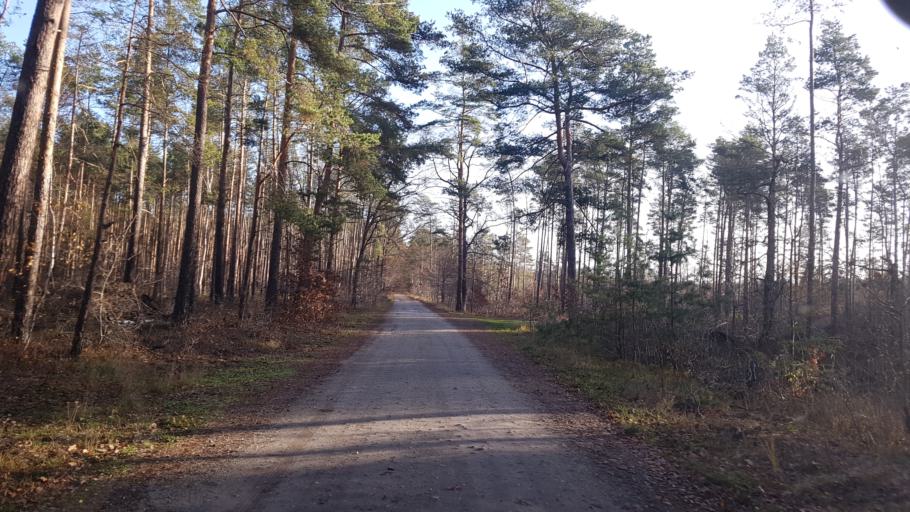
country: DE
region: Brandenburg
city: Ruckersdorf
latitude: 51.5924
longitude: 13.5791
